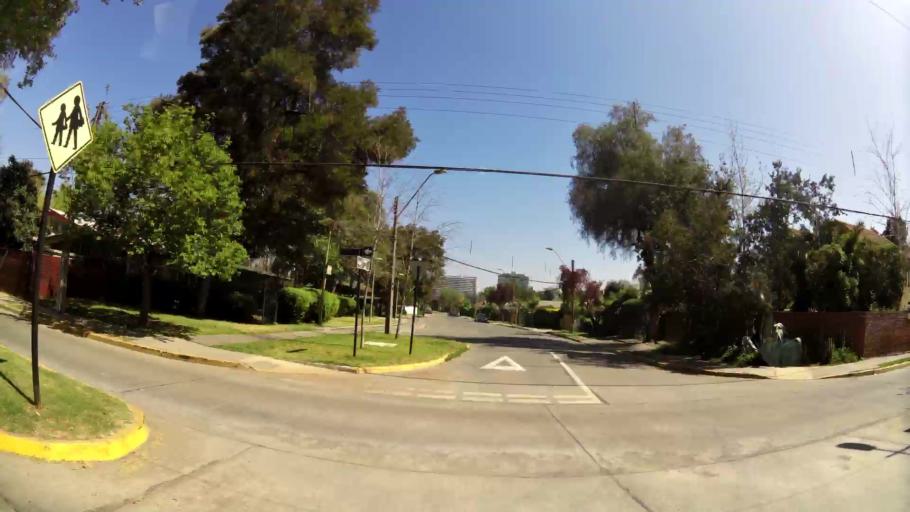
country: CL
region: Santiago Metropolitan
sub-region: Provincia de Santiago
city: Villa Presidente Frei, Nunoa, Santiago, Chile
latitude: -33.4195
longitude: -70.5463
